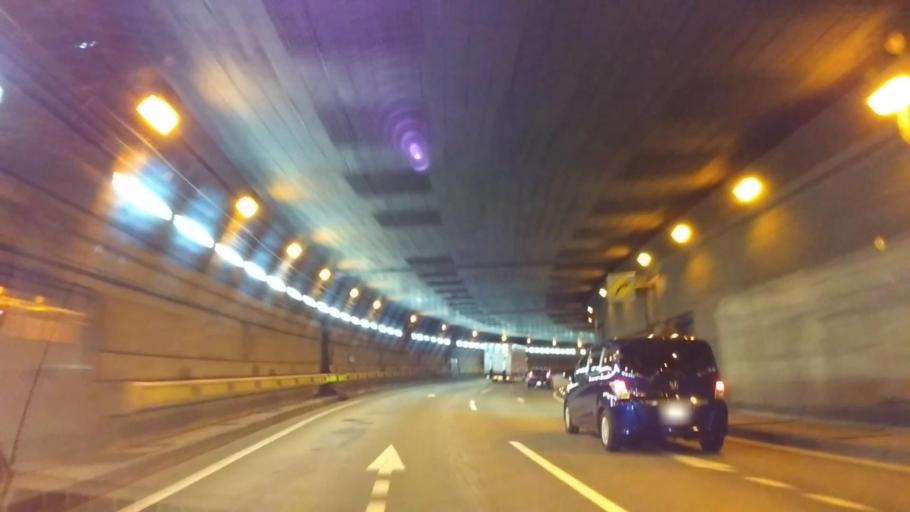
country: JP
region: Kanagawa
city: Minami-rinkan
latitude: 35.4889
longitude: 139.4623
